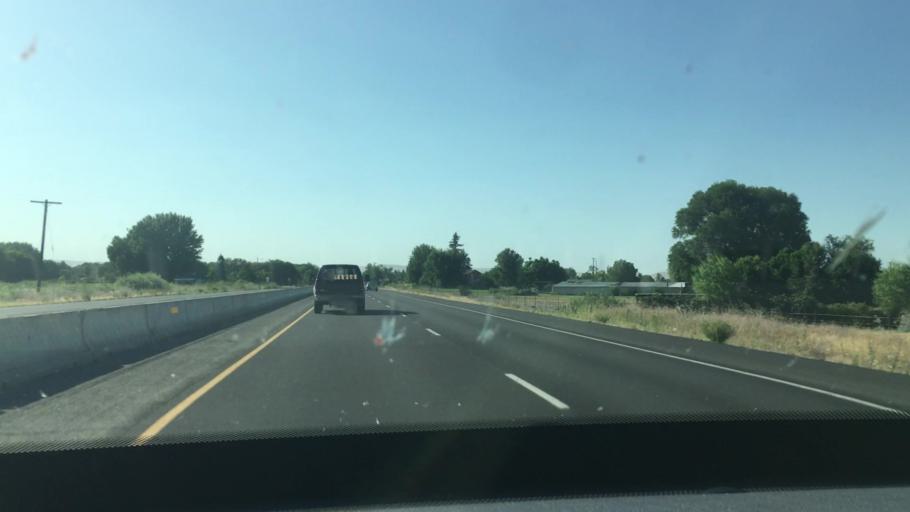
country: US
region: Washington
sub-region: Yakima County
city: Wapato
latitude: 46.4112
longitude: -120.3881
